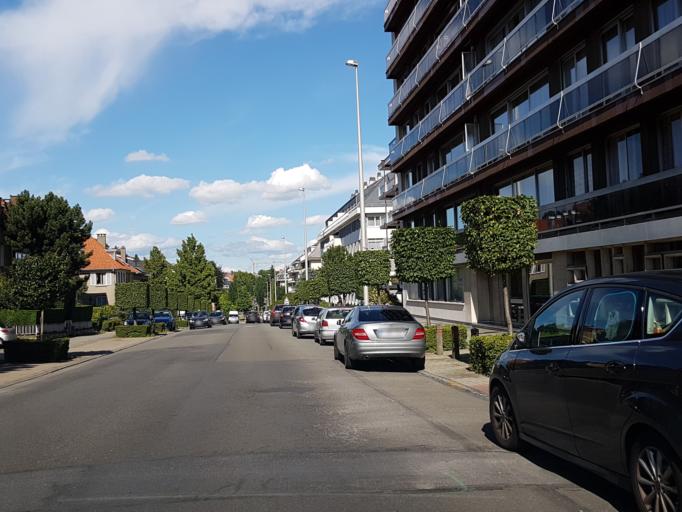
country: BE
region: Brussels Capital
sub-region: Bruxelles-Capitale
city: Brussels
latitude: 50.8293
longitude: 4.4094
